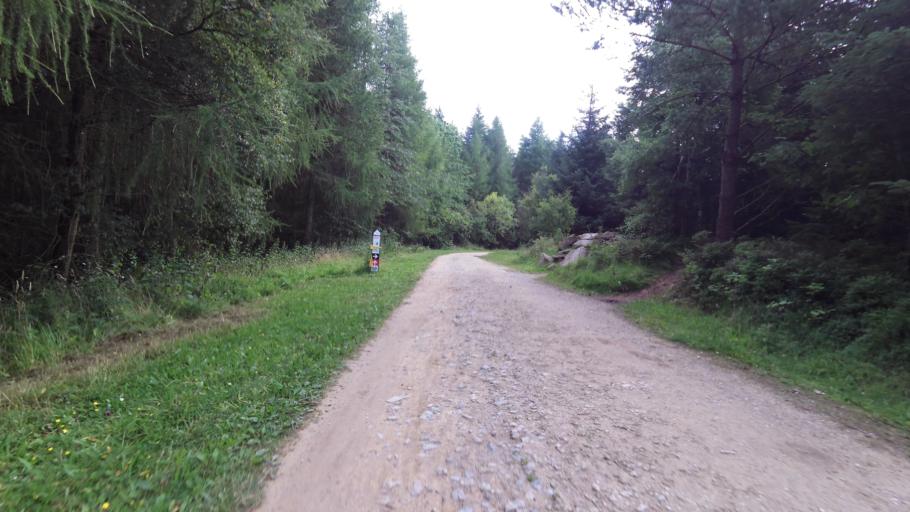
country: GB
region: England
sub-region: North Yorkshire
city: Thornton Dale
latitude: 54.2976
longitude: -0.6380
